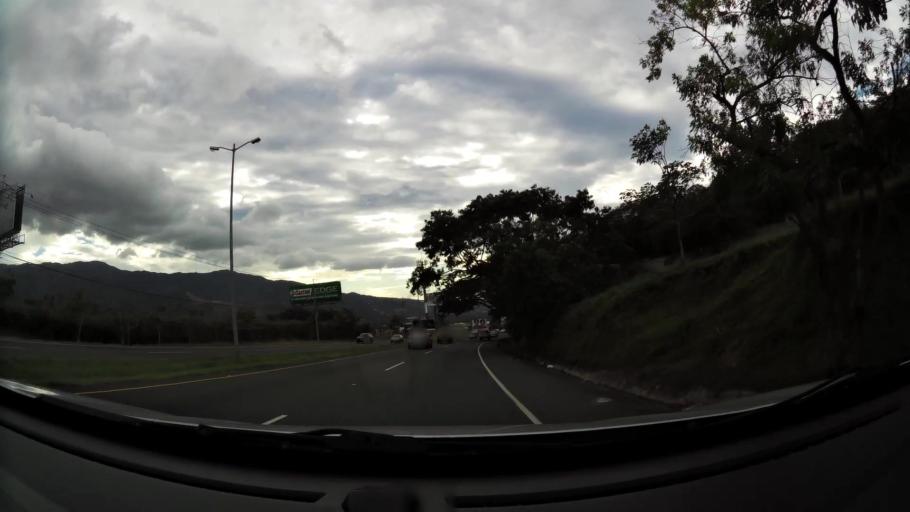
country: CR
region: San Jose
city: Santa Ana
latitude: 9.9438
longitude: -84.1685
